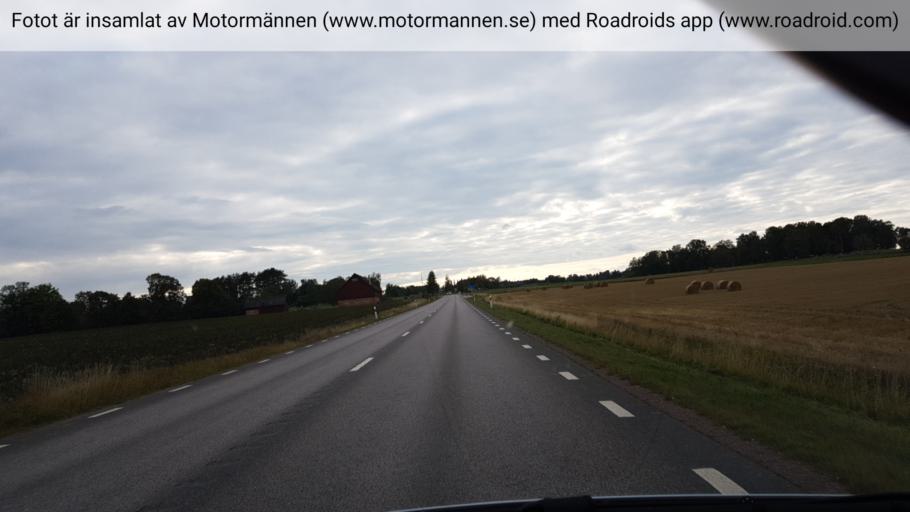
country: SE
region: Vaestra Goetaland
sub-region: Tidaholms Kommun
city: Olofstorp
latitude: 58.3527
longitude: 14.0635
